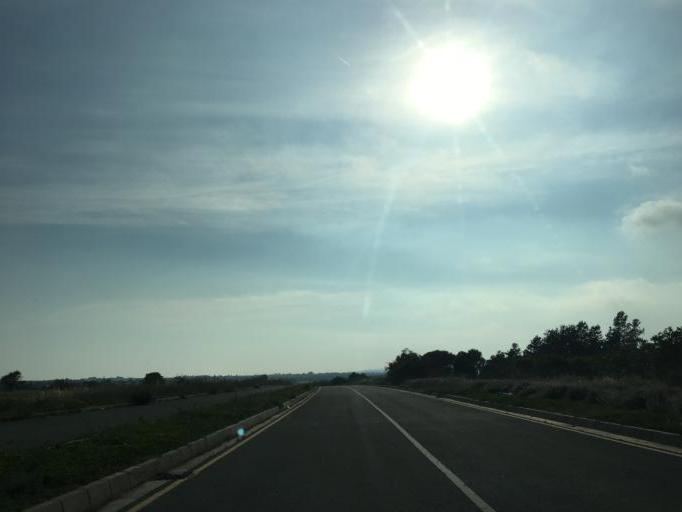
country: CY
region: Larnaka
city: Tersefanou
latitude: 34.7938
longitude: 33.5073
